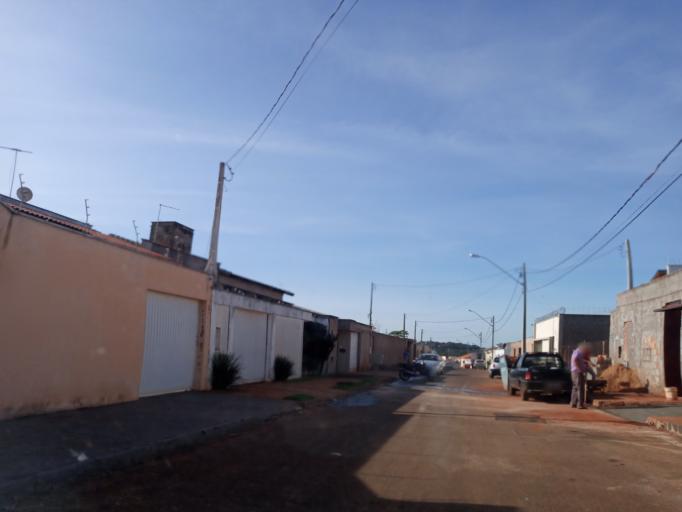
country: BR
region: Minas Gerais
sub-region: Ituiutaba
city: Ituiutaba
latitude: -18.9658
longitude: -49.4402
